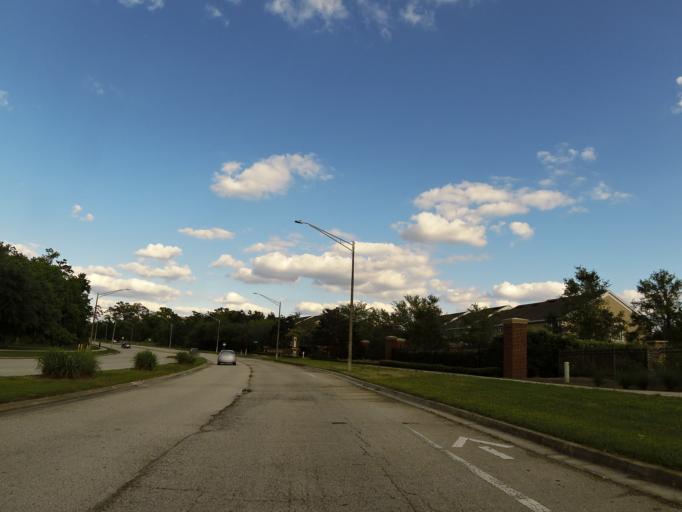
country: US
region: Florida
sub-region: Duval County
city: Jacksonville
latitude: 30.2540
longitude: -81.5780
